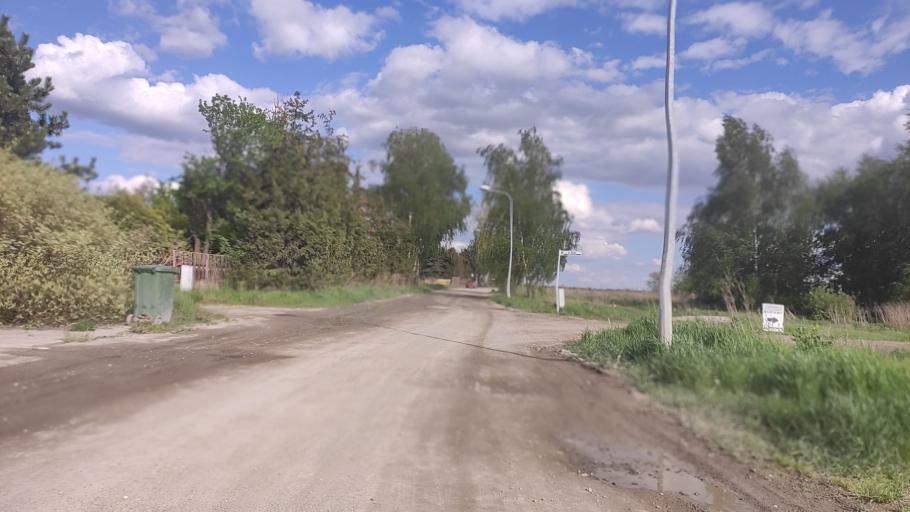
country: PL
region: Greater Poland Voivodeship
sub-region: Powiat poznanski
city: Swarzedz
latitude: 52.3893
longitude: 17.1244
